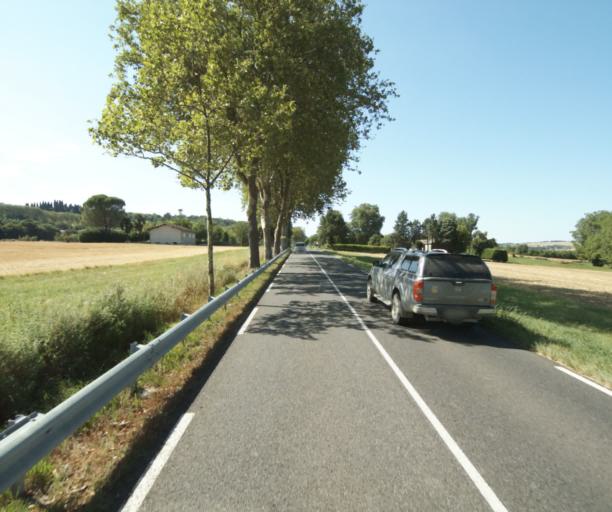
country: FR
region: Midi-Pyrenees
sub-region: Departement de la Haute-Garonne
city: Saint-Felix-Lauragais
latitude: 43.4874
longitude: 1.9080
